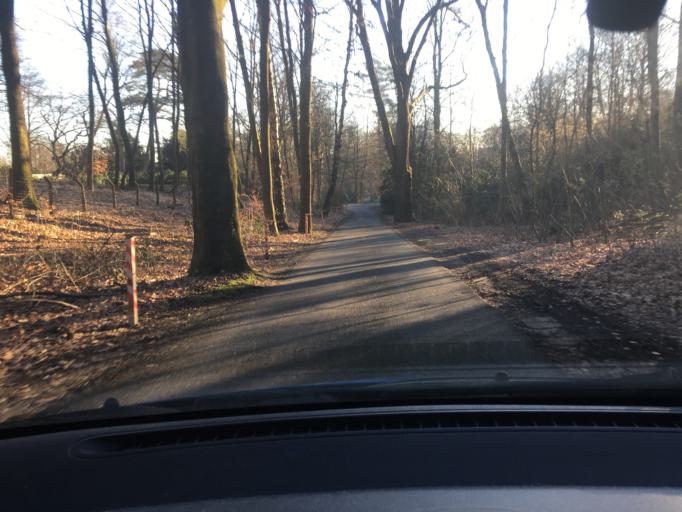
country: DE
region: Lower Saxony
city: Seevetal
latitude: 53.3943
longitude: 9.9534
